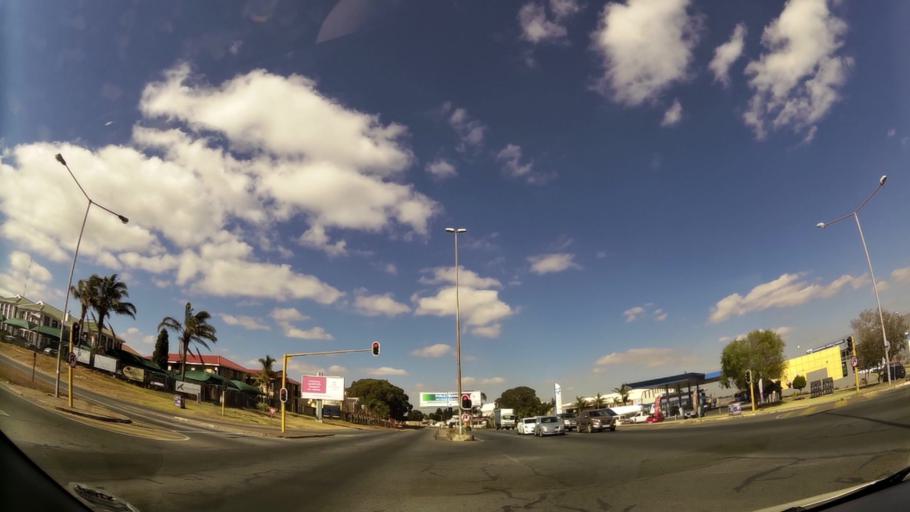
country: ZA
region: Gauteng
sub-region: West Rand District Municipality
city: Krugersdorp
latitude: -26.1103
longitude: 27.8043
